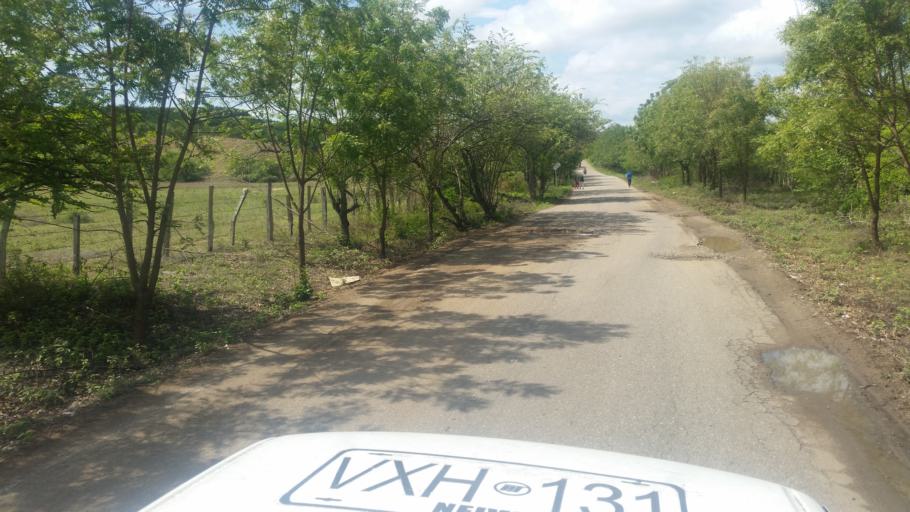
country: CO
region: Huila
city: Villavieja
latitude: 3.2016
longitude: -75.2097
